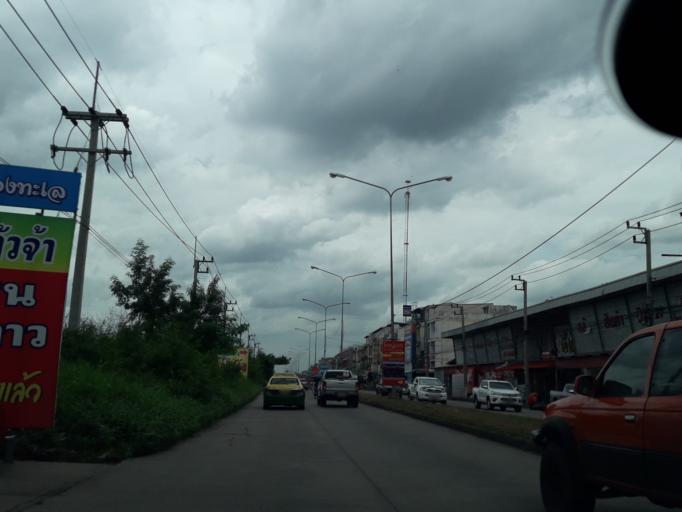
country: TH
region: Pathum Thani
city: Khlong Luang
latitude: 14.0691
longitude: 100.6339
